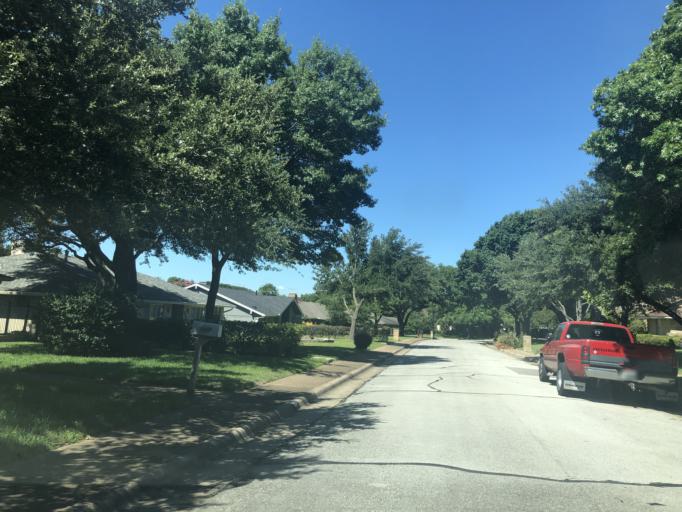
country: US
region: Texas
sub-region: Dallas County
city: Duncanville
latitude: 32.6386
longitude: -96.9289
